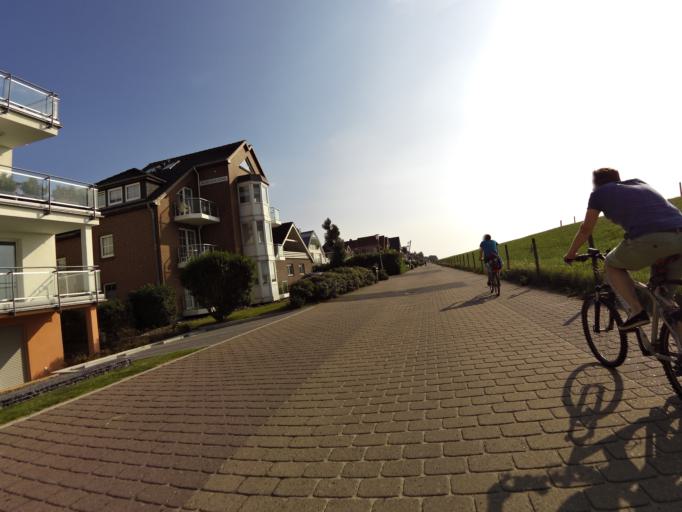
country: DE
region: Lower Saxony
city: Cuxhaven
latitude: 53.8816
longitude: 8.6276
